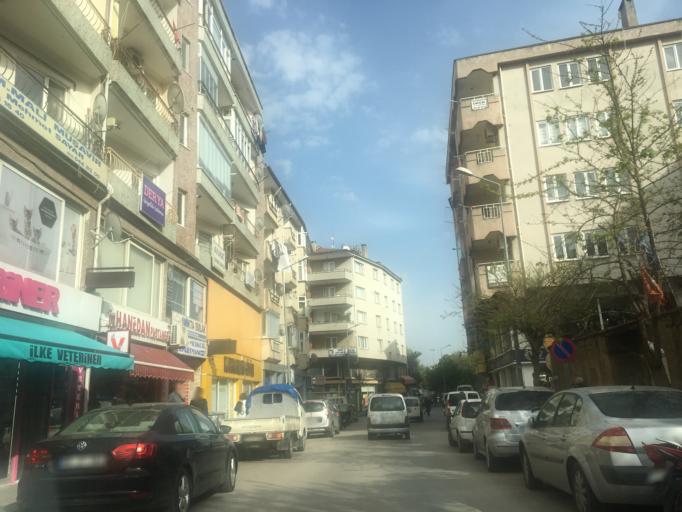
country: TR
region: Bursa
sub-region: Mudanya
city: Mudanya
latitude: 40.3745
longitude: 28.8864
